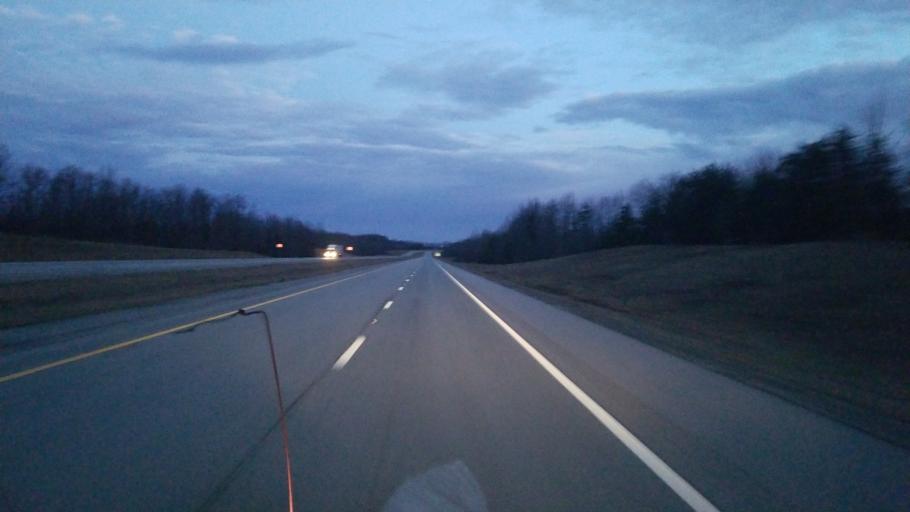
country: US
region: Tennessee
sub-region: Van Buren County
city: Spencer
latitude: 35.6099
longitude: -85.4707
